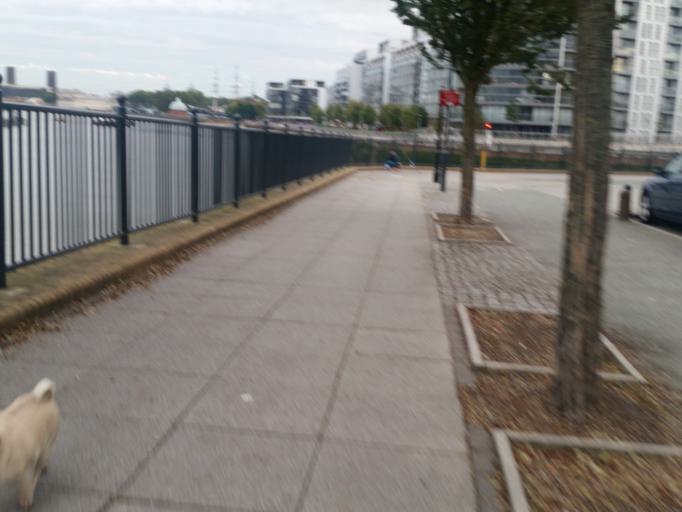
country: GB
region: England
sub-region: Greater London
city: Poplar
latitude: 51.4835
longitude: -0.0193
